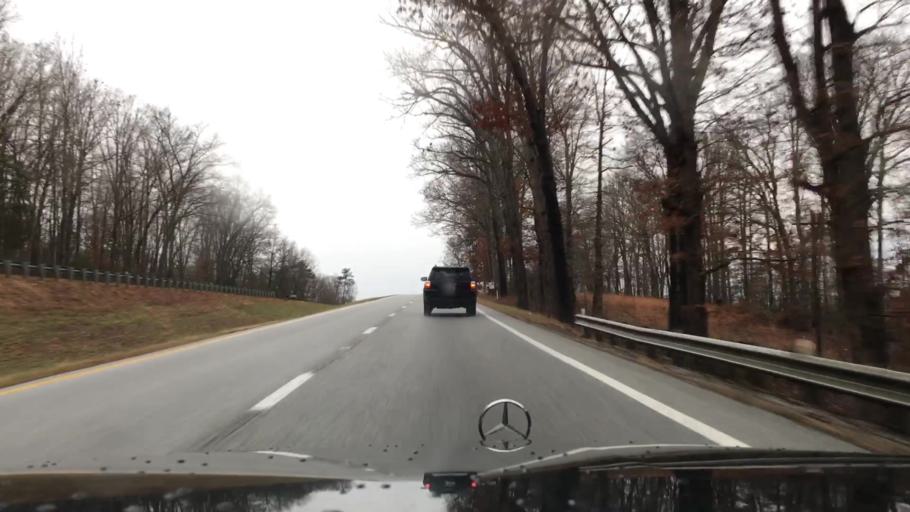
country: US
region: Virginia
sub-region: Nelson County
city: Nellysford
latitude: 37.8333
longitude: -78.8337
